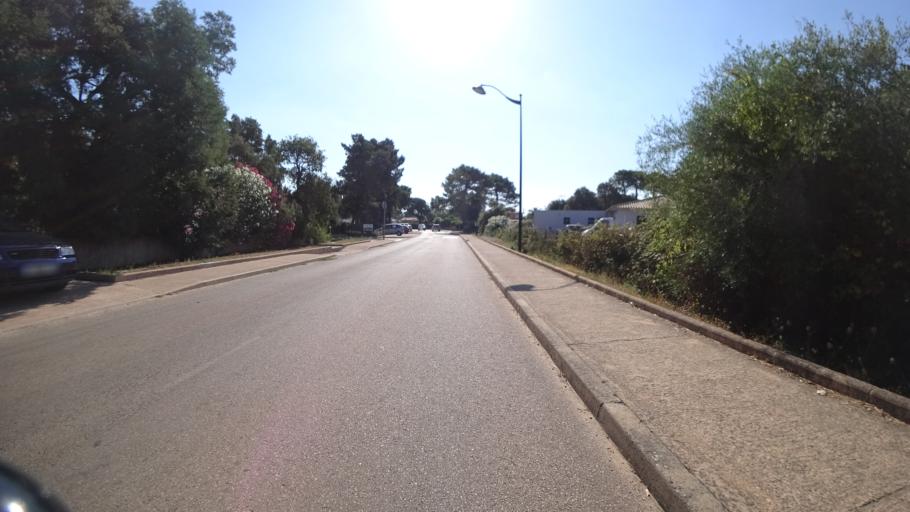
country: FR
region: Corsica
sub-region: Departement de la Corse-du-Sud
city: Porto-Vecchio
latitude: 41.6380
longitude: 9.3408
